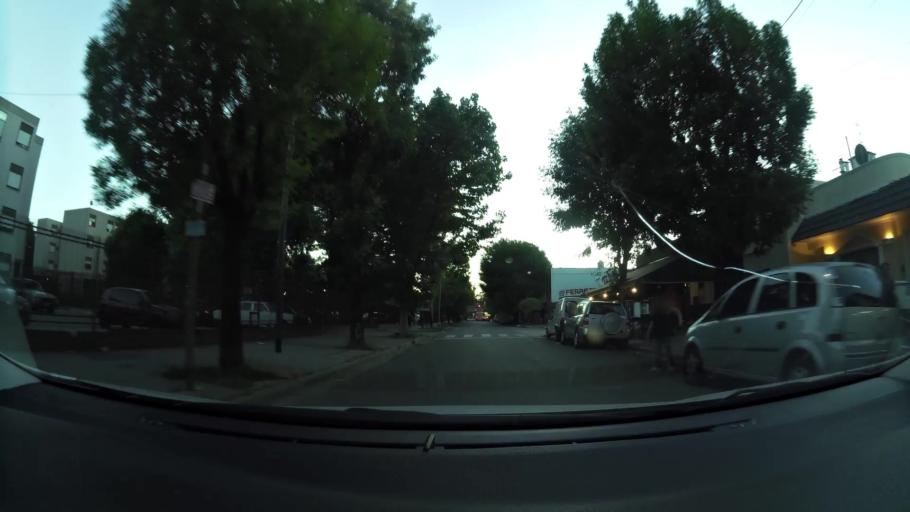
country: AR
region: Buenos Aires F.D.
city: Villa Lugano
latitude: -34.6830
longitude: -58.4720
